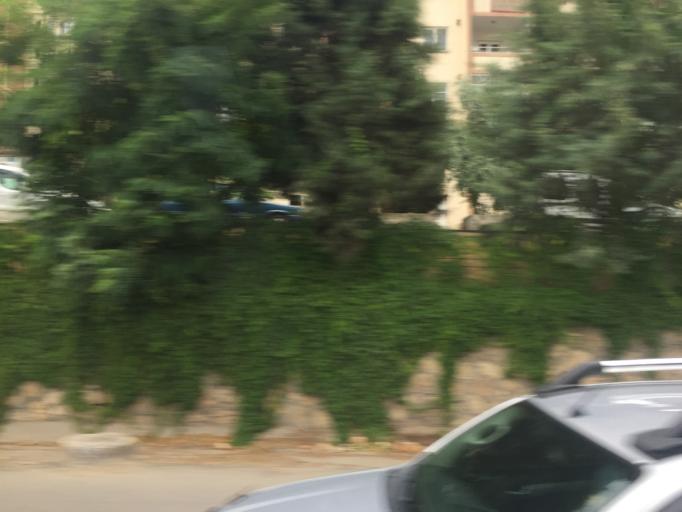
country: TR
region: Gaziantep
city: Gaziantep
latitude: 37.0471
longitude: 37.4235
